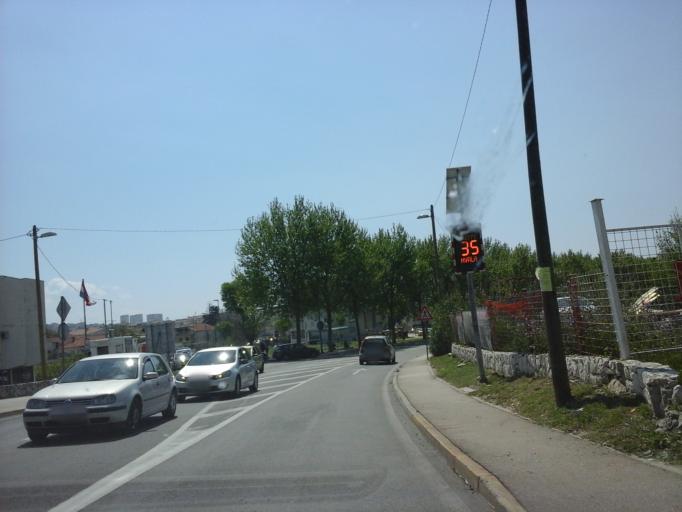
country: HR
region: Splitsko-Dalmatinska
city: Solin
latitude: 43.5415
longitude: 16.4916
